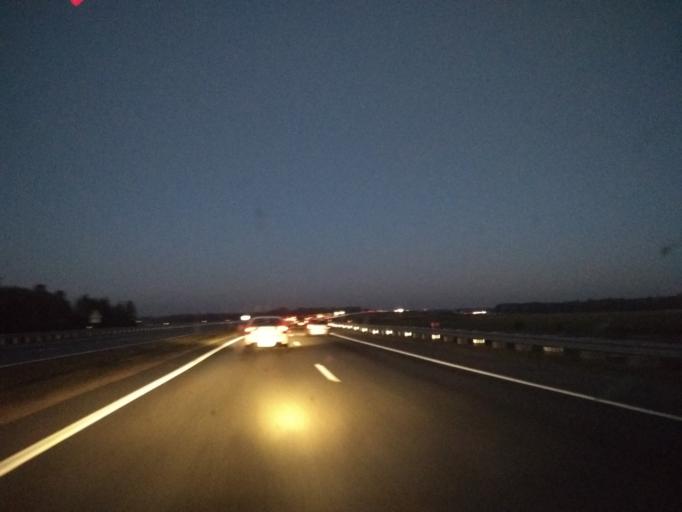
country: BY
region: Minsk
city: Dzyarzhynsk
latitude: 53.6571
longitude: 27.0858
